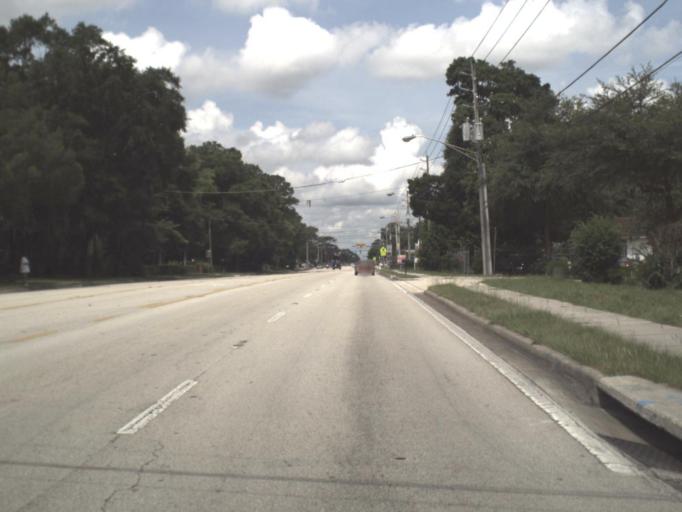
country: US
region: Florida
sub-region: Duval County
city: Jacksonville
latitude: 30.4389
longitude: -81.6895
